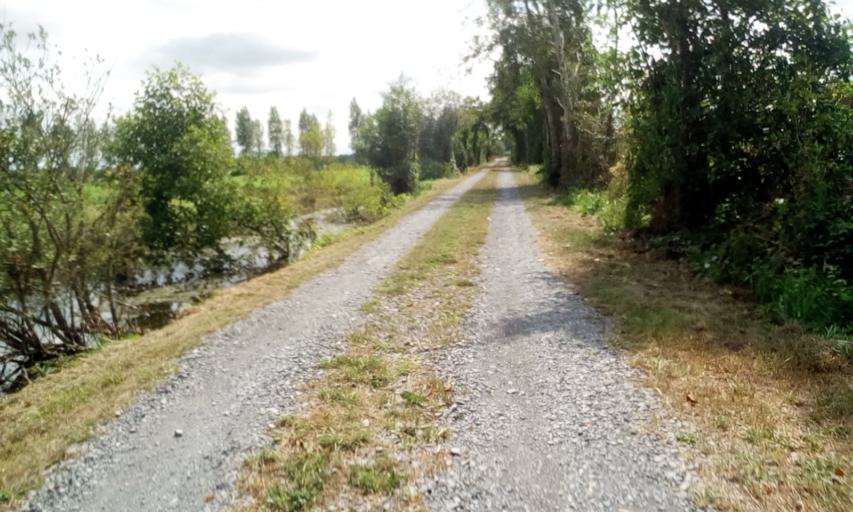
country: FR
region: Lower Normandy
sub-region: Departement du Calvados
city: Bavent
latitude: 49.2289
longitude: -0.1708
